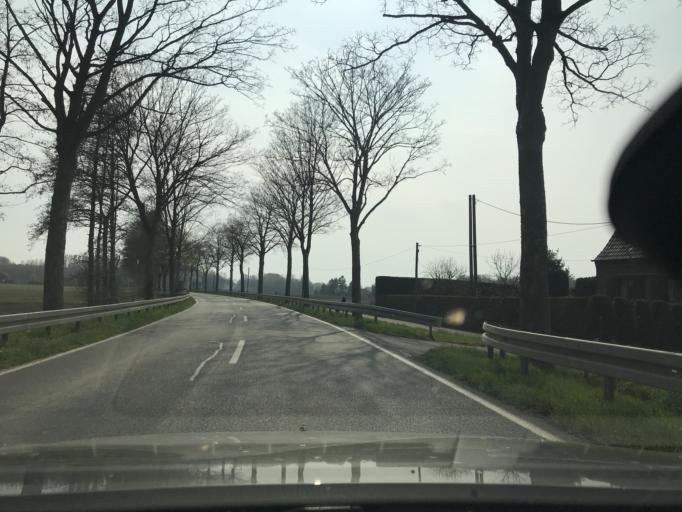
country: DE
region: North Rhine-Westphalia
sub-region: Regierungsbezirk Dusseldorf
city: Wachtendonk
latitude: 51.4634
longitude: 6.3512
